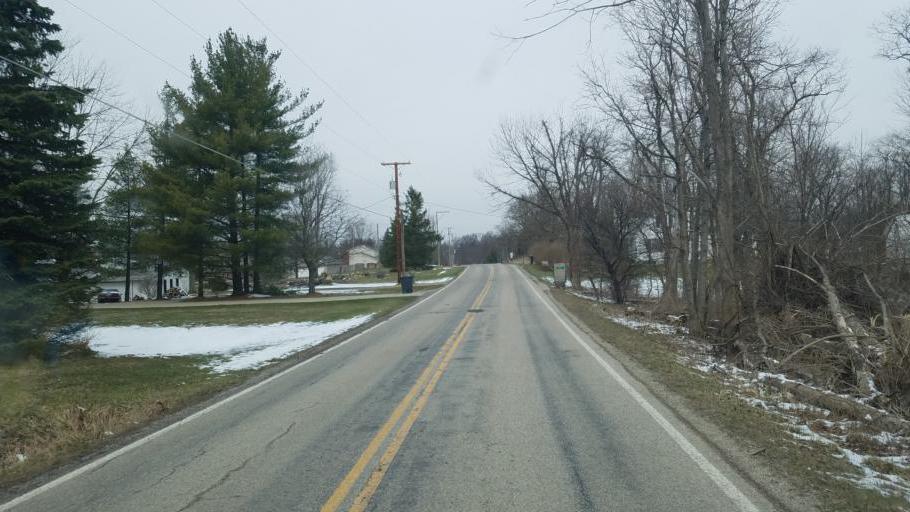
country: US
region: Ohio
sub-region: Richland County
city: Ontario
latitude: 40.7283
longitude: -82.6170
